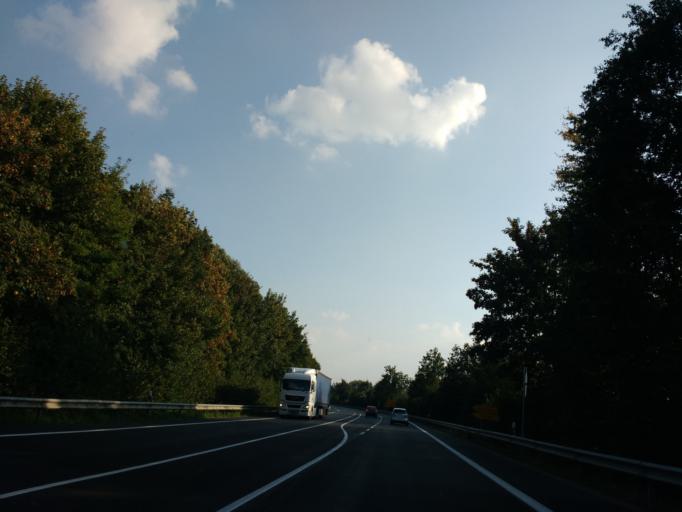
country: DE
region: North Rhine-Westphalia
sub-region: Regierungsbezirk Detmold
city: Steinheim
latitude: 51.8996
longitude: 9.0860
